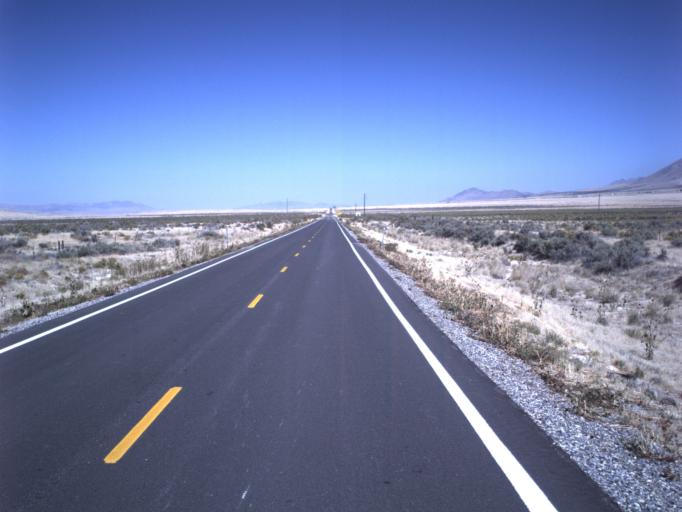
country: US
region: Utah
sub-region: Tooele County
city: Grantsville
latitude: 40.3411
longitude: -112.7448
